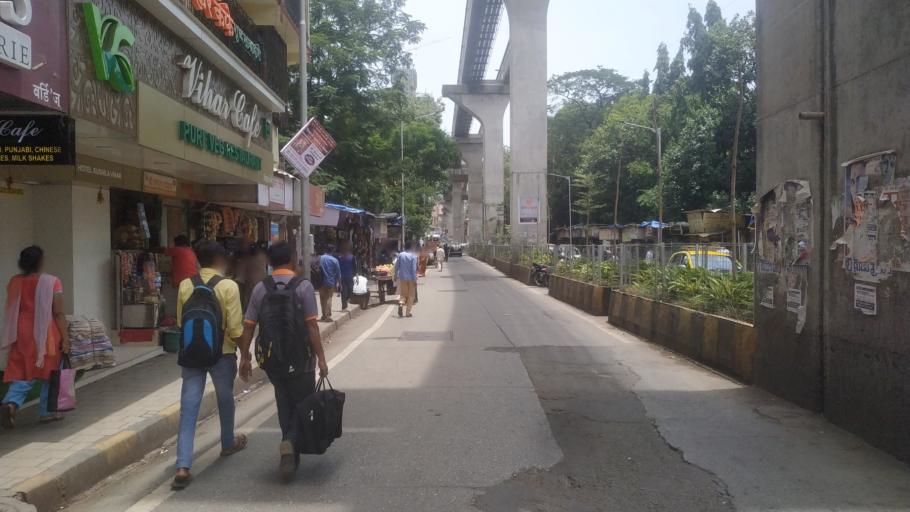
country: IN
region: Maharashtra
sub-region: Mumbai Suburban
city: Mumbai
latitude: 18.9954
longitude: 72.8363
